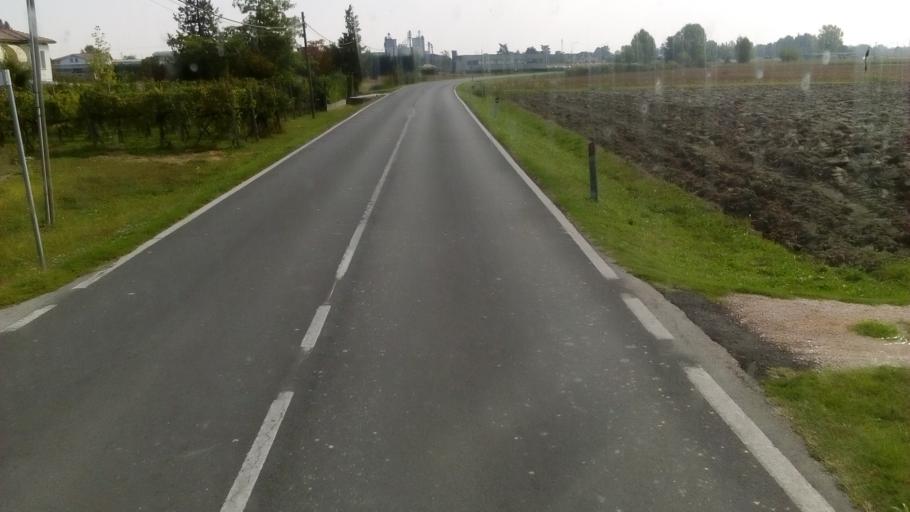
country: IT
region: Veneto
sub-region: Provincia di Rovigo
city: Castelnovo Bariano
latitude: 45.0418
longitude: 11.2887
